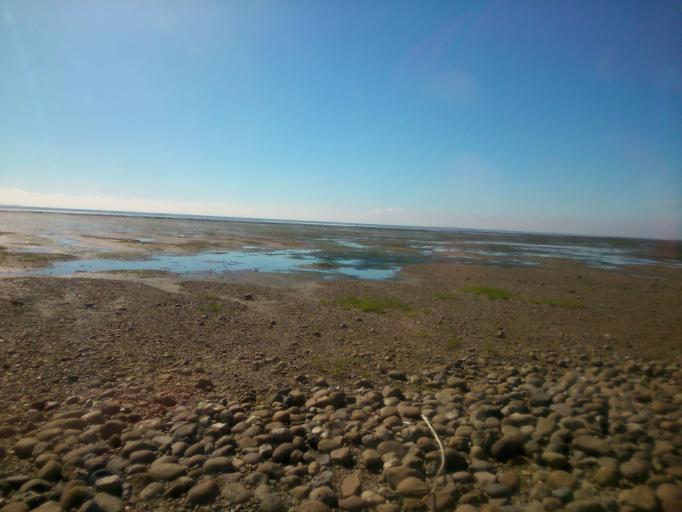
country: DK
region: South Denmark
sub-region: Esbjerg Kommune
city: Tjaereborg
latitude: 55.2938
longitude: 8.5995
